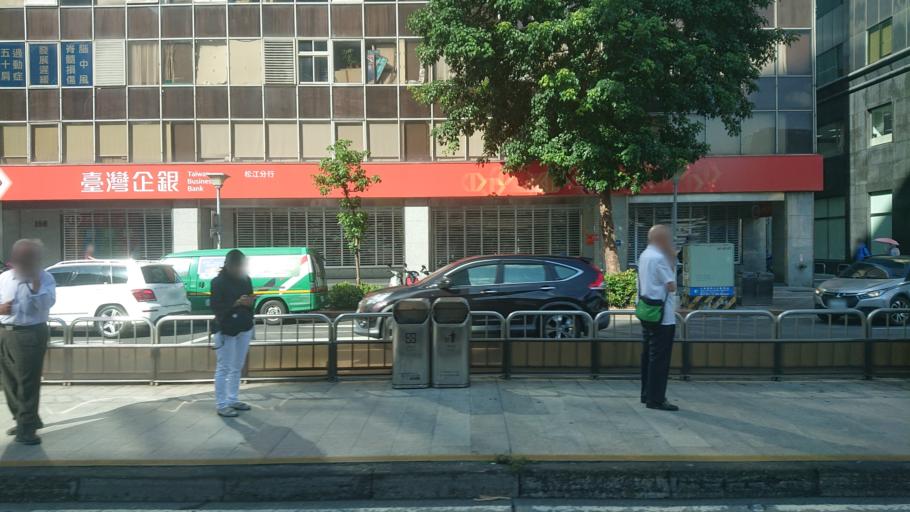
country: TW
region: Taipei
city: Taipei
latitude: 25.0551
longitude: 121.5331
